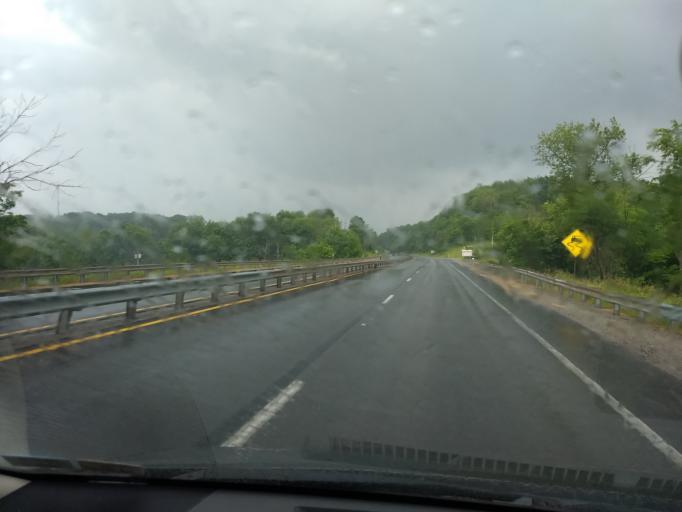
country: US
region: Pennsylvania
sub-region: Armstrong County
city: Apollo
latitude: 40.5321
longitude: -79.6159
